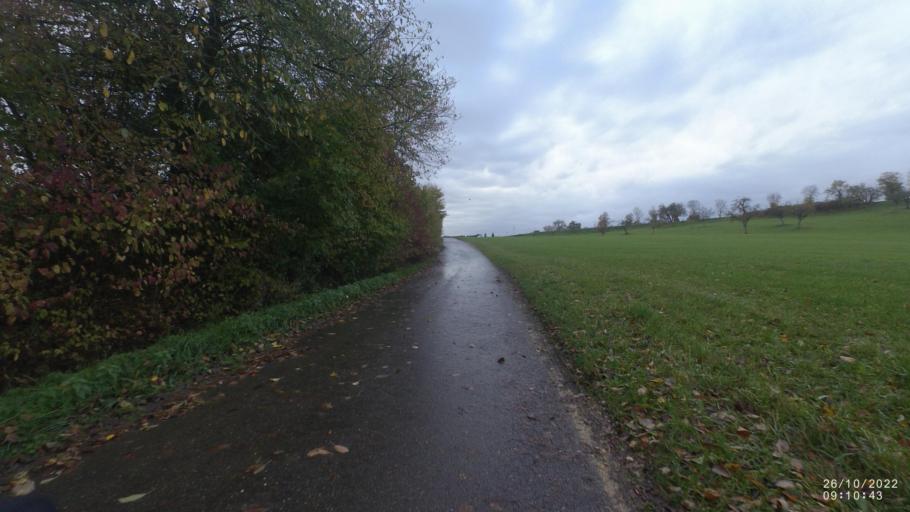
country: DE
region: Baden-Wuerttemberg
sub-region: Regierungsbezirk Stuttgart
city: Heiningen
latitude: 48.6764
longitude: 9.6619
